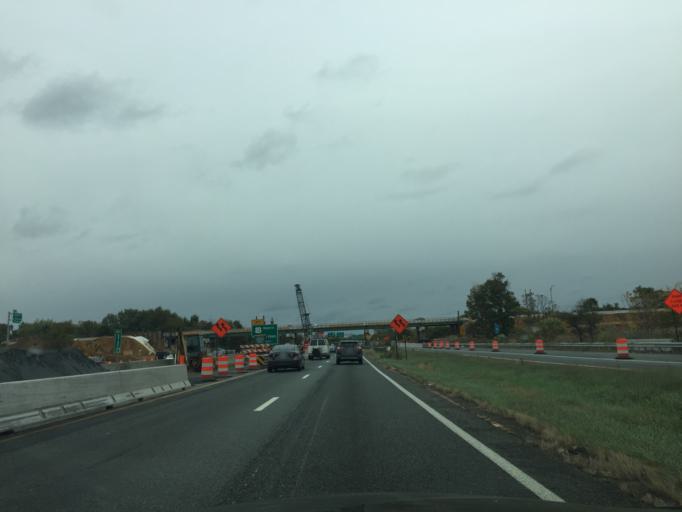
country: US
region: Delaware
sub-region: New Castle County
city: Newport
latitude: 39.6998
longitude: -75.6035
